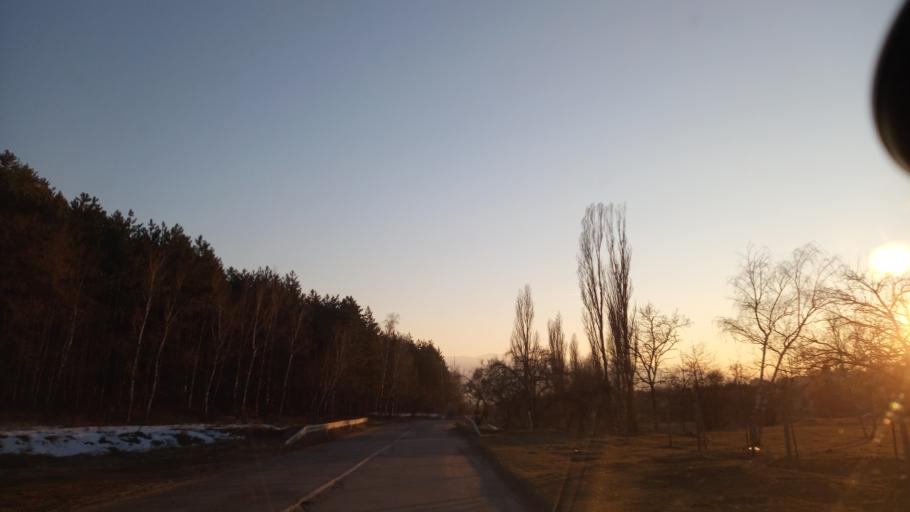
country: BG
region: Sofia-Capital
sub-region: Stolichna Obshtina
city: Bukhovo
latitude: 42.7874
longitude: 23.5221
